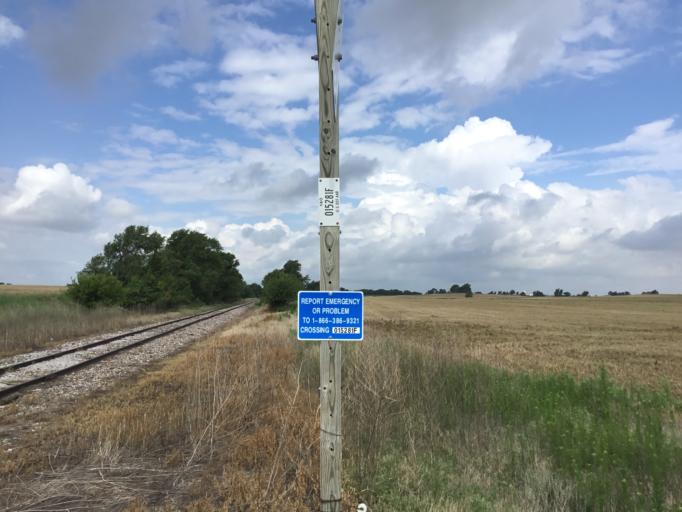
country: US
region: Kansas
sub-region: Pratt County
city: Pratt
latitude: 37.6379
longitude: -98.6840
